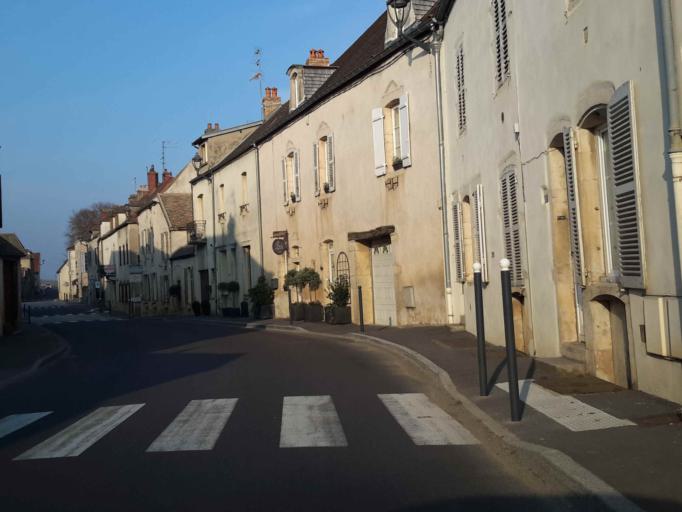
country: FR
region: Bourgogne
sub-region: Departement de la Cote-d'Or
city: Bligny-les-Beaune
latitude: 47.0072
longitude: 4.7961
